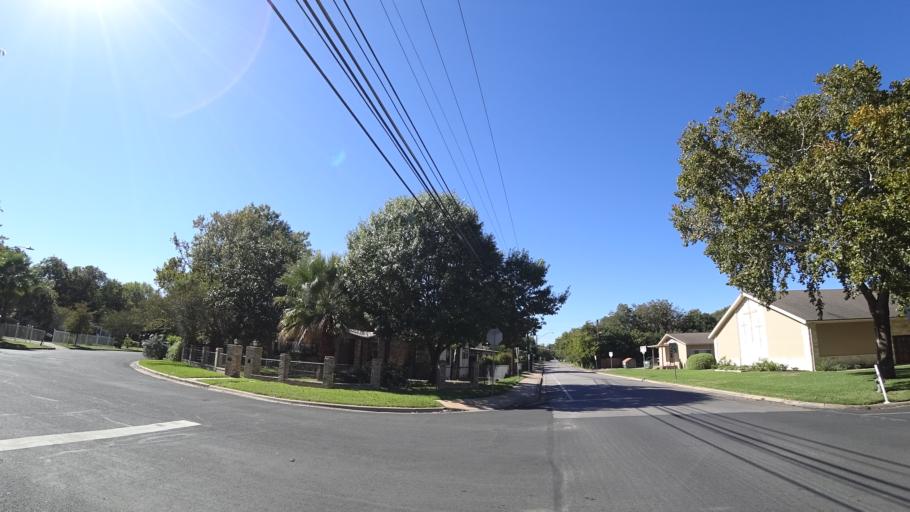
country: US
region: Texas
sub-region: Travis County
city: Rollingwood
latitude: 30.2234
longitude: -97.7822
